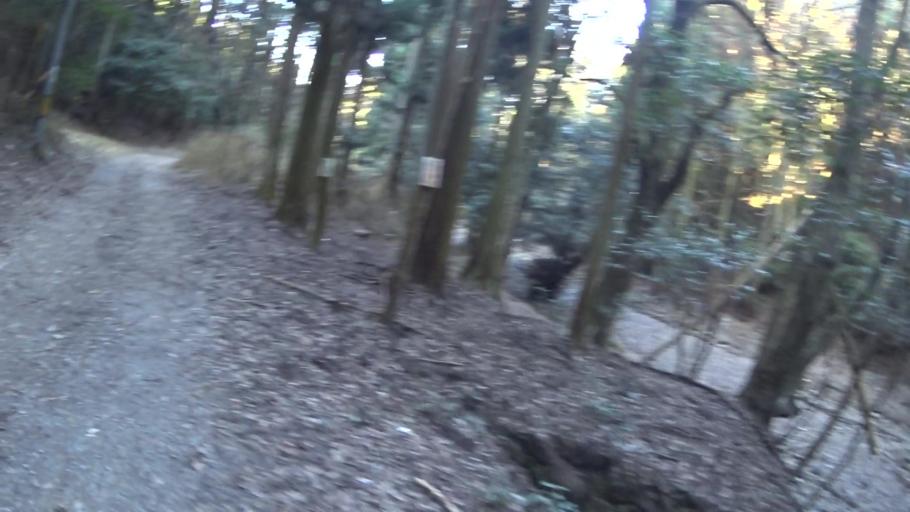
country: JP
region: Kyoto
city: Uji
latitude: 34.9510
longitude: 135.8268
